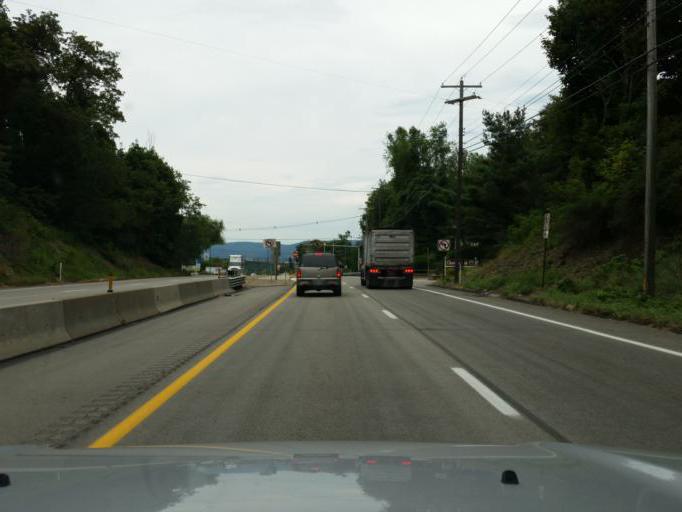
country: US
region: Pennsylvania
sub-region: Westmoreland County
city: Greensburg
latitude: 40.2916
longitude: -79.4670
